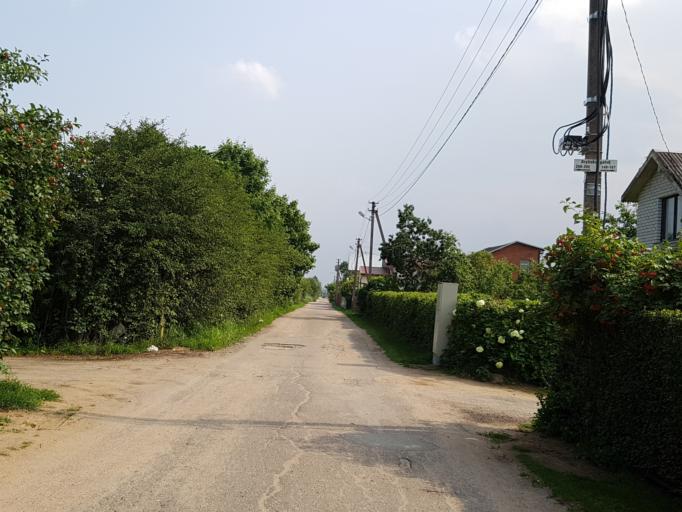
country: LT
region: Vilnius County
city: Rasos
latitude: 54.7912
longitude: 25.3646
